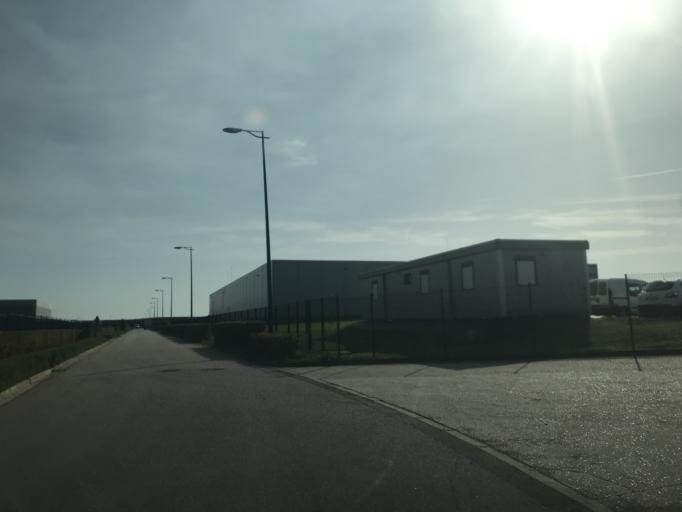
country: FR
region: Haute-Normandie
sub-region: Departement de l'Eure
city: Saint-Aubin-sur-Gaillon
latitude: 49.1428
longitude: 1.3069
